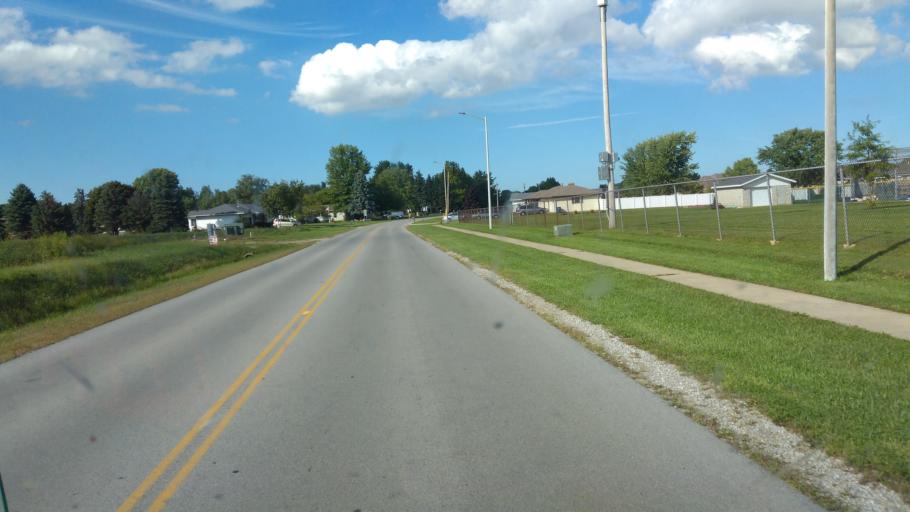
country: US
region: Ohio
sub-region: Sandusky County
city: Clyde
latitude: 41.2914
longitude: -82.9905
